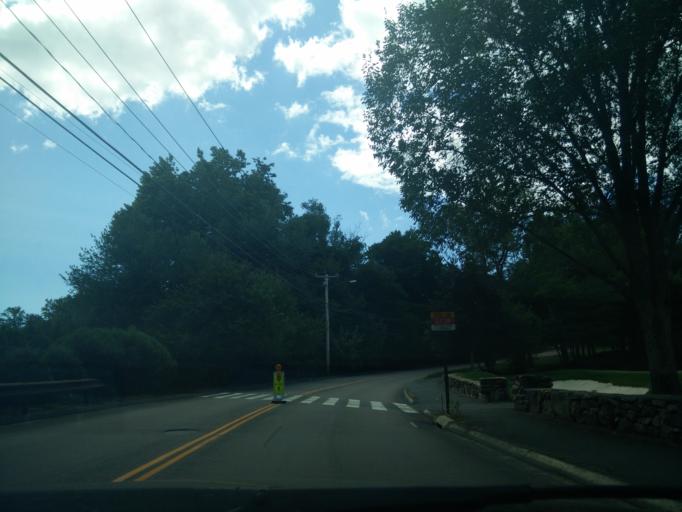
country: US
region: Connecticut
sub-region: Fairfield County
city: Bridgeport
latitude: 41.1923
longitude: -73.2285
